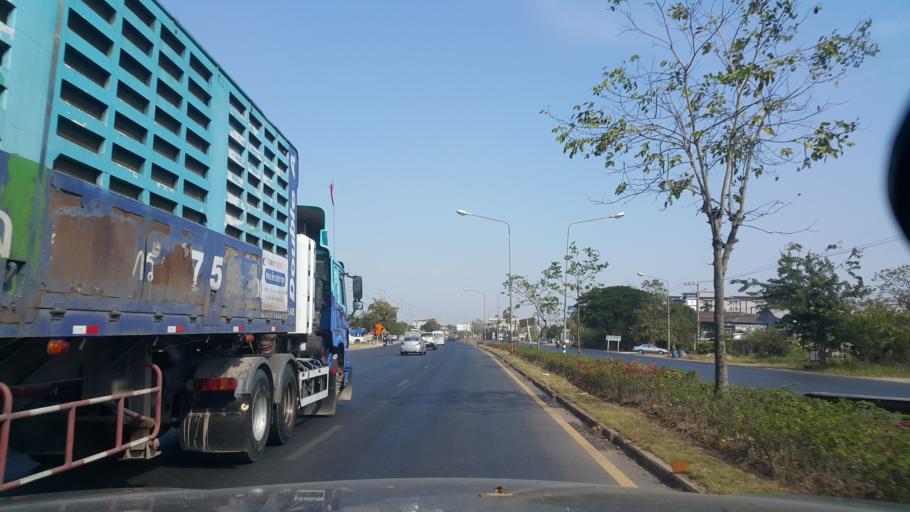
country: TH
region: Nakhon Ratchasima
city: Nakhon Ratchasima
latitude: 14.9704
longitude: 102.0523
